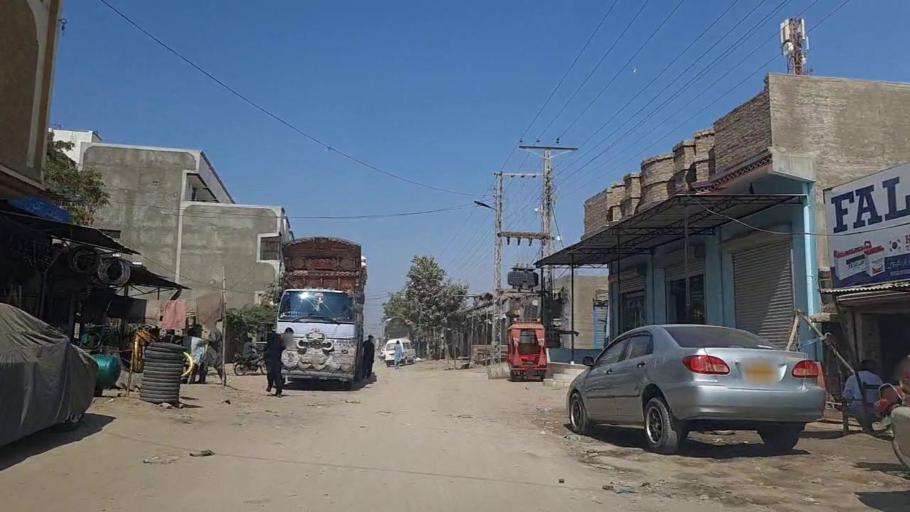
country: PK
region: Sindh
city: Naukot
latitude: 24.8591
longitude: 69.4037
